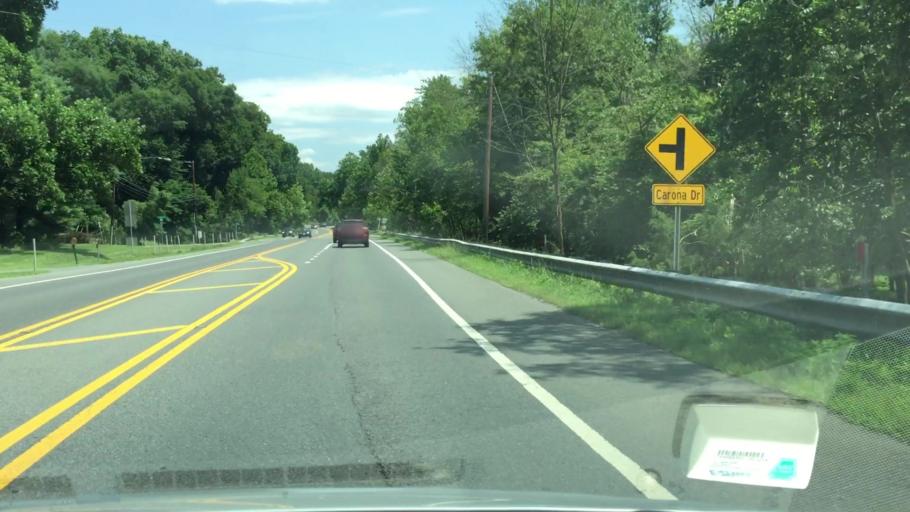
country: US
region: Maryland
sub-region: Montgomery County
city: Layhill
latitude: 39.0946
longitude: -77.0287
